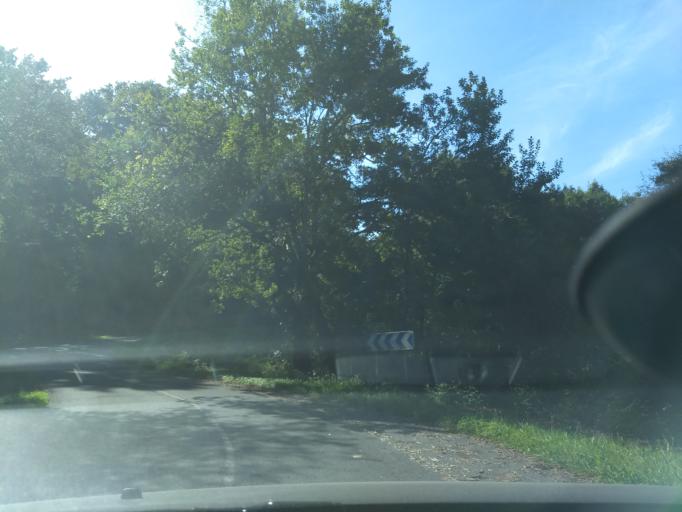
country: FR
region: Aquitaine
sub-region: Departement des Pyrenees-Atlantiques
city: Soumoulou
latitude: 43.2912
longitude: -0.1479
